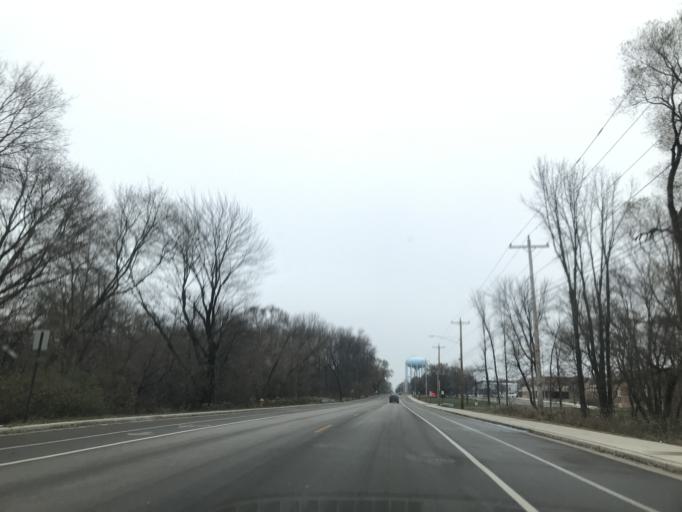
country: US
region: Wisconsin
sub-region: Marinette County
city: Marinette
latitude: 45.0845
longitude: -87.6296
